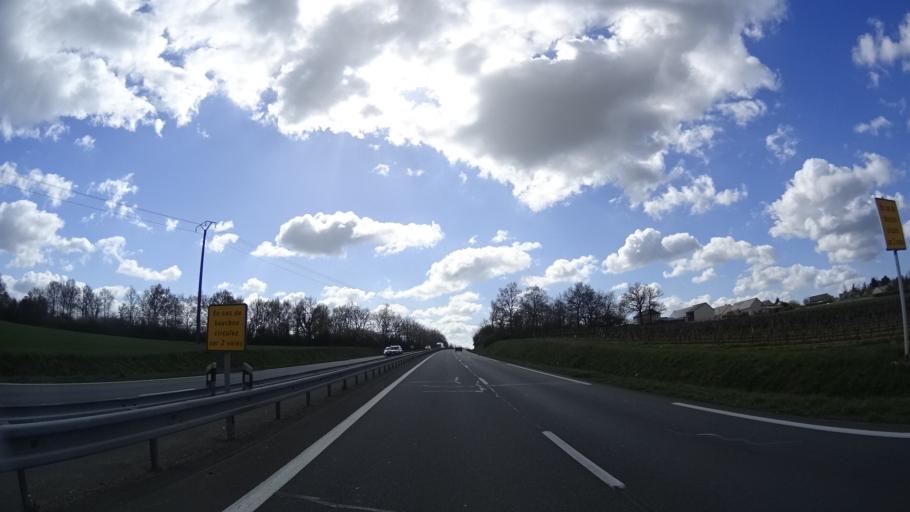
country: FR
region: Pays de la Loire
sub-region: Departement de Maine-et-Loire
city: Brissac-Quince
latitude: 47.3543
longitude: -0.4399
